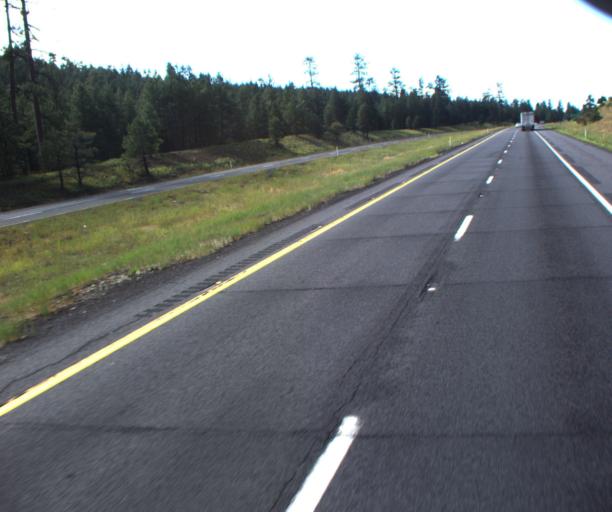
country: US
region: Arizona
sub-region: Coconino County
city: Mountainaire
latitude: 35.0377
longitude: -111.6848
